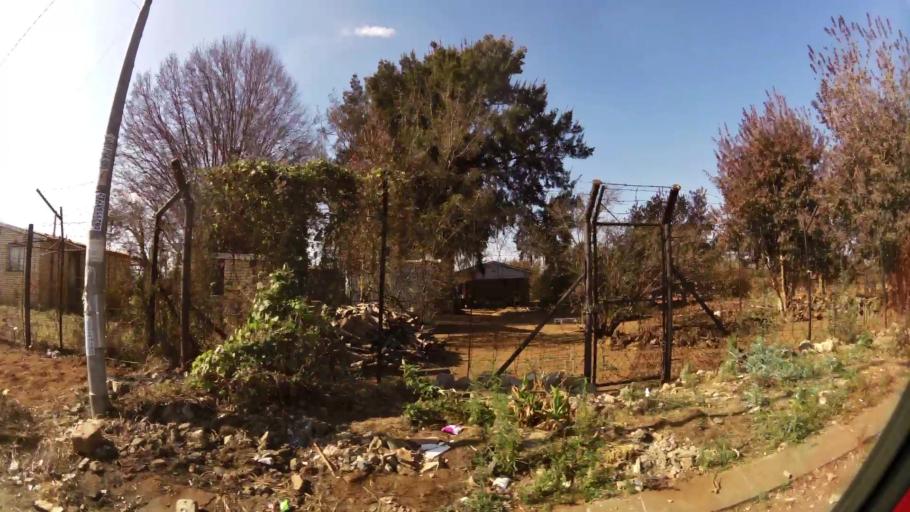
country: ZA
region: Gauteng
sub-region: City of Johannesburg Metropolitan Municipality
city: Soweto
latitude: -26.2364
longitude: 27.8801
